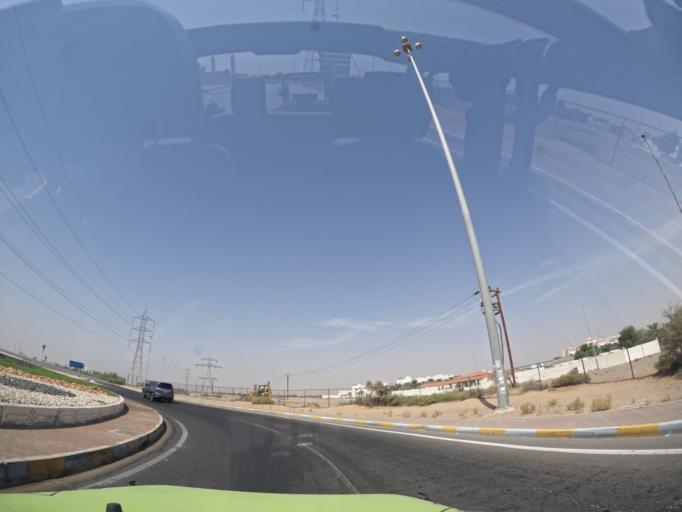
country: AE
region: Abu Dhabi
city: Al Ain
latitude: 24.2063
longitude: 55.3869
